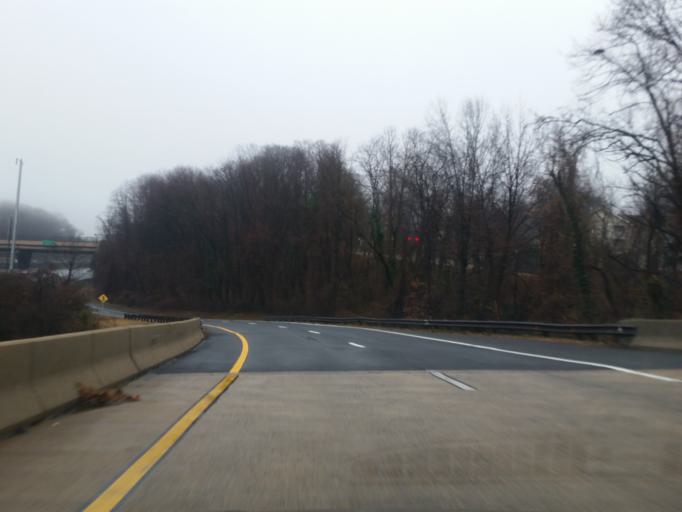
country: US
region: Virginia
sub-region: Fairfax County
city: Pimmit Hills
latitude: 38.9002
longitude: -77.1871
